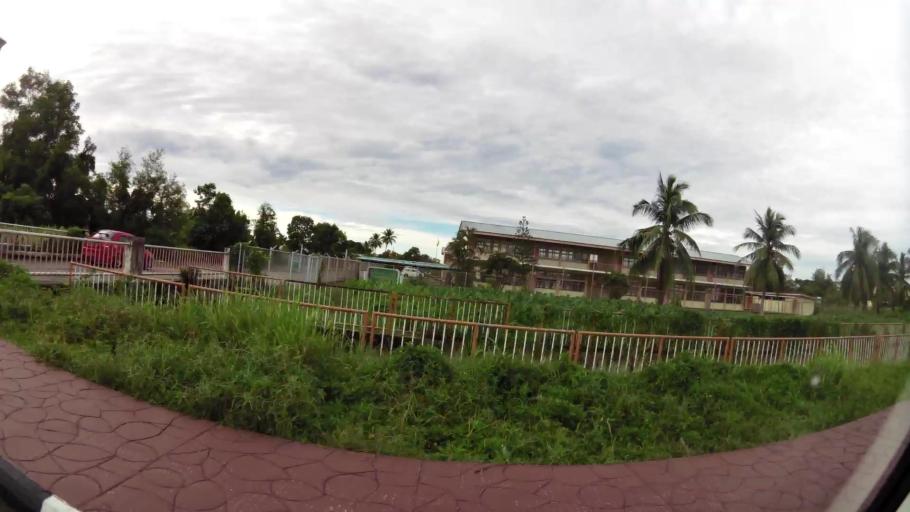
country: BN
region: Belait
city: Seria
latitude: 4.6075
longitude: 114.3294
